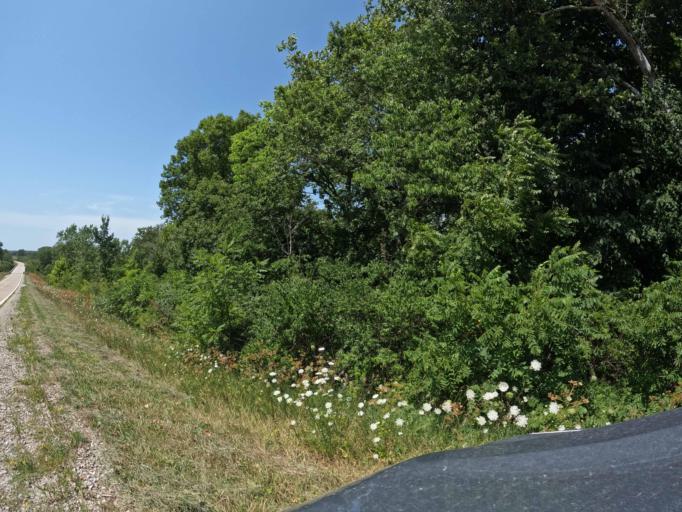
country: US
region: Iowa
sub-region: Henry County
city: Mount Pleasant
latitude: 40.9881
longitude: -91.6532
